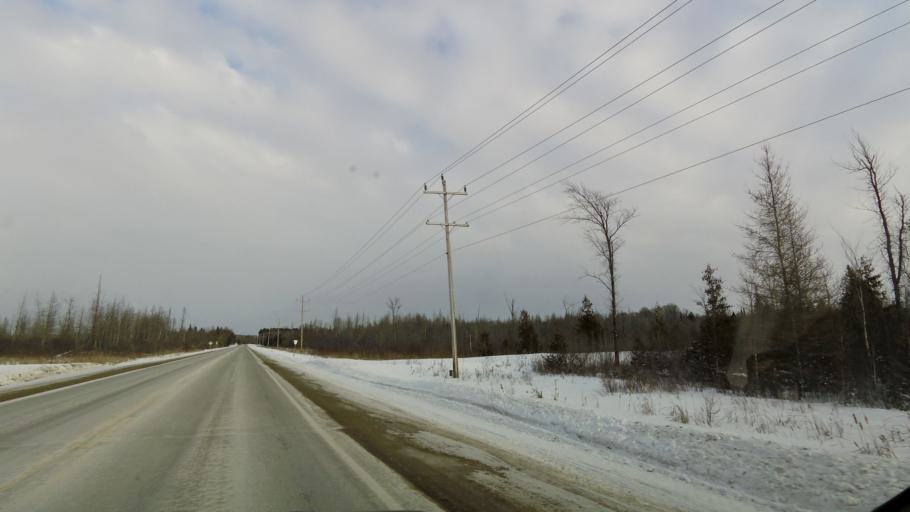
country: CA
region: Ontario
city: Uxbridge
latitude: 44.4715
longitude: -78.9361
